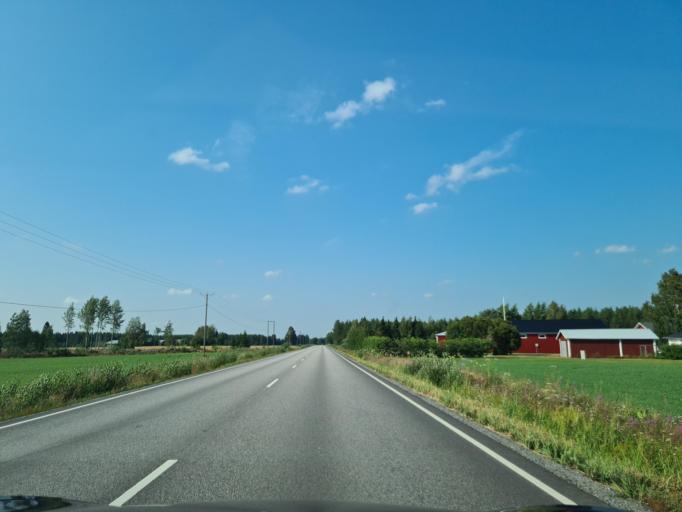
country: FI
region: Satakunta
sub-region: Pohjois-Satakunta
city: Karvia
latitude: 62.0461
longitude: 22.5143
